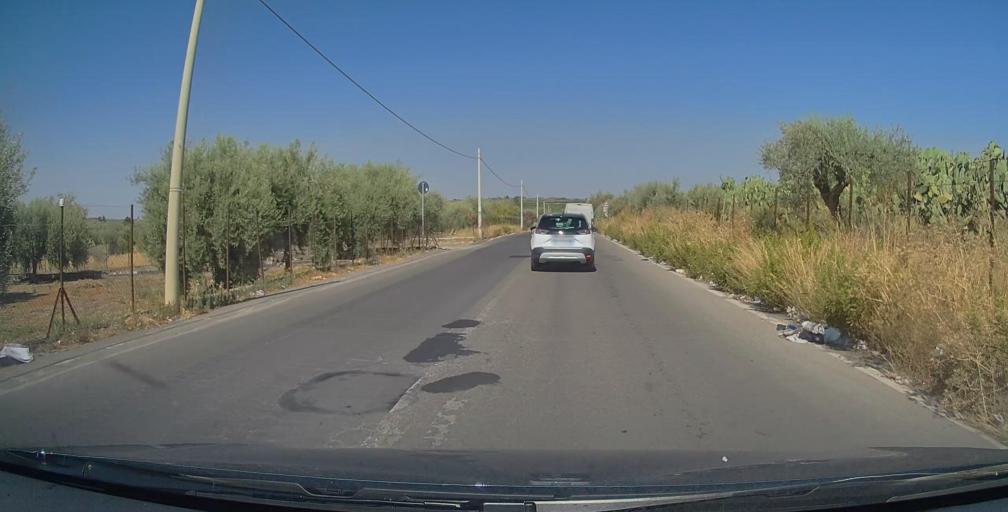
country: IT
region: Sicily
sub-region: Catania
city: Palazzolo
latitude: 37.5486
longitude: 14.9371
